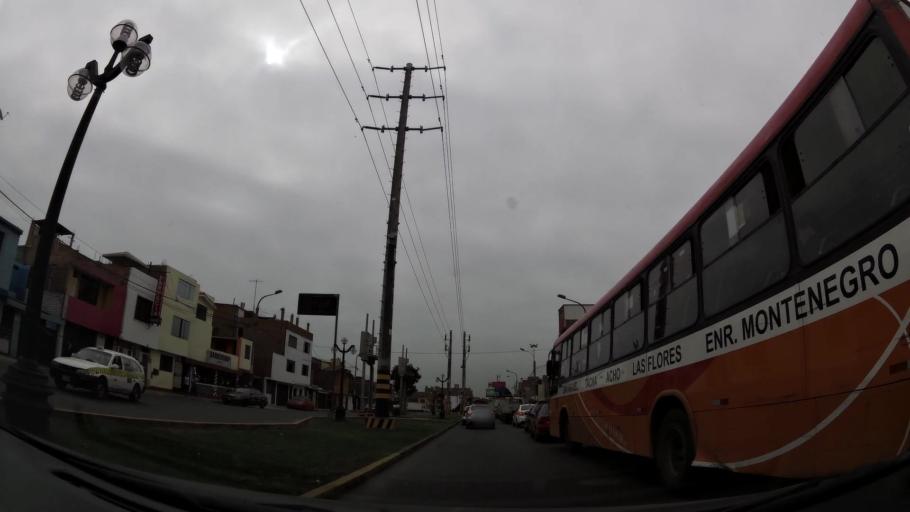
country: PE
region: Callao
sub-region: Callao
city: Callao
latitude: -12.0566
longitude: -77.1055
